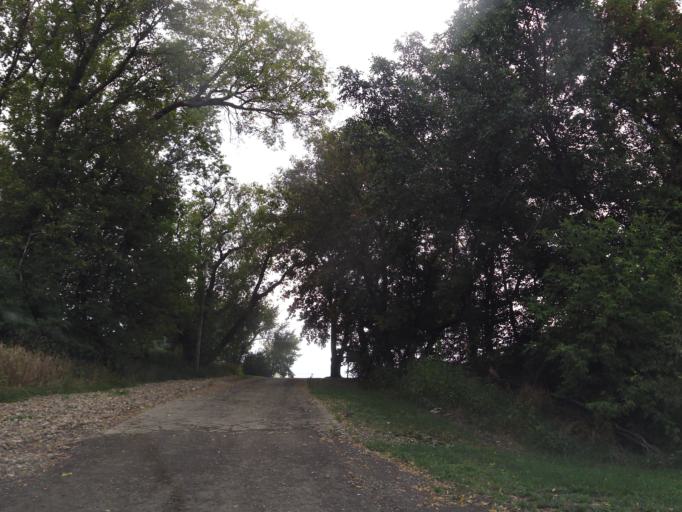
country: US
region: North Dakota
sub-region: Walsh County
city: Grafton
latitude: 48.5606
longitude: -97.1761
